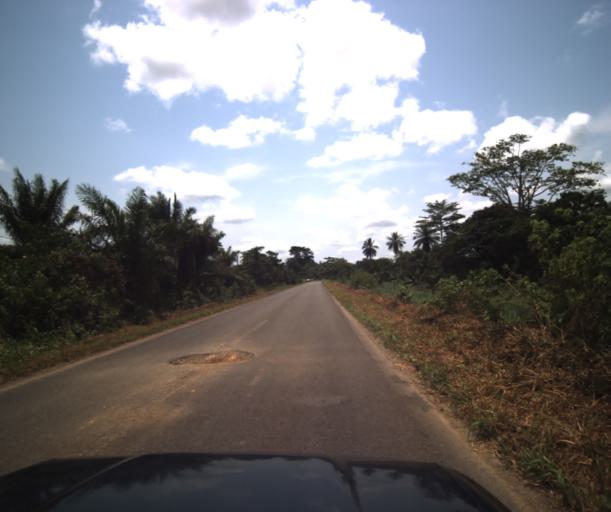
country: CM
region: Centre
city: Eseka
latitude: 3.6990
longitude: 10.7864
